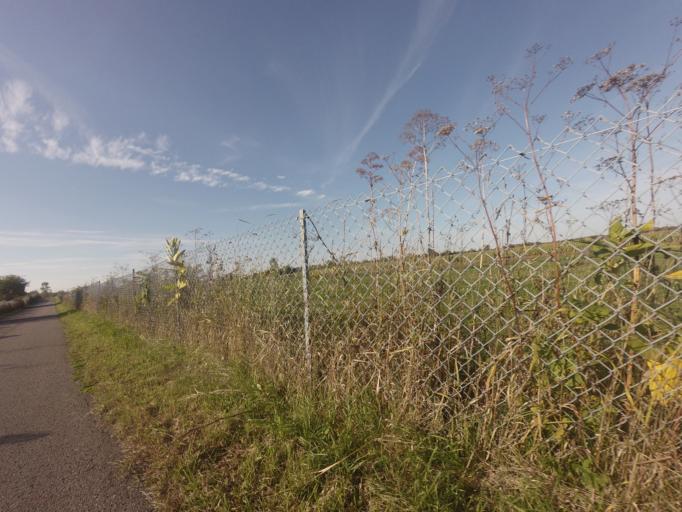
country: CA
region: Quebec
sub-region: Laurentides
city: Saint-Jerome
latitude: 45.7495
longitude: -73.9710
